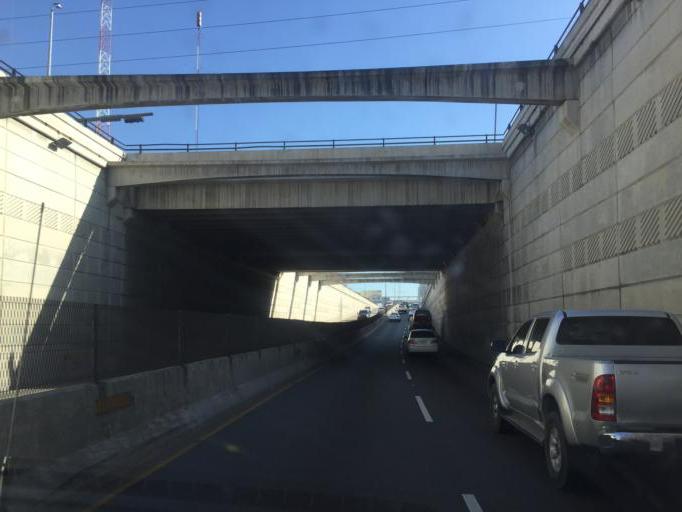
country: DO
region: Nacional
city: Bella Vista
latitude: 18.4576
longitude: -69.9482
